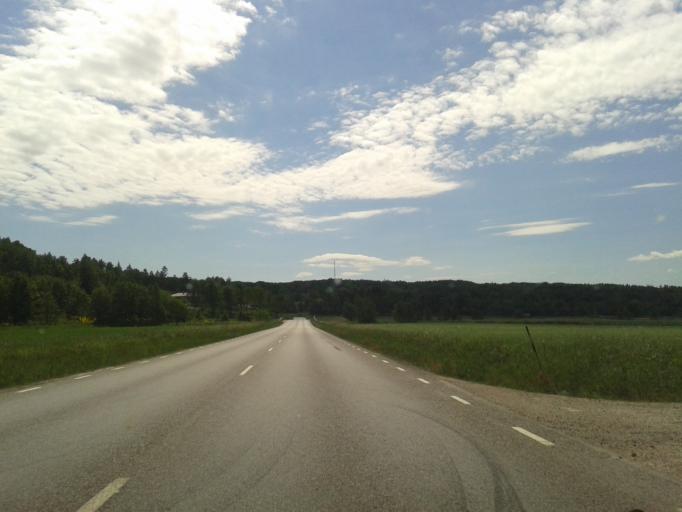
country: SE
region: Vaestra Goetaland
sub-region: Uddevalla Kommun
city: Ljungskile
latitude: 58.2824
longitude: 11.8904
